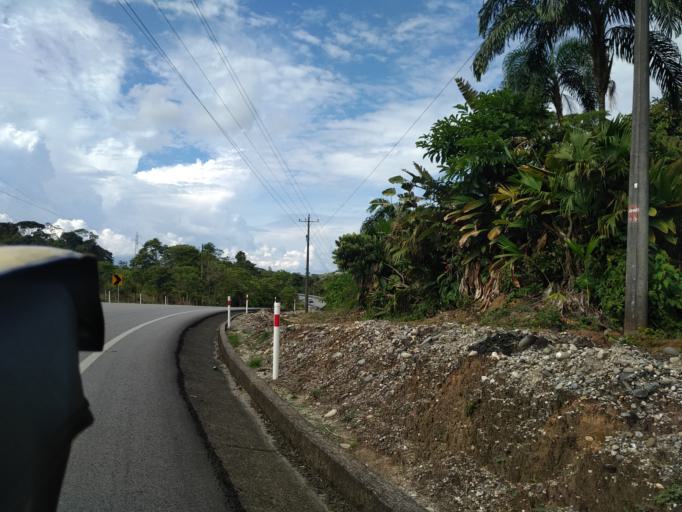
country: EC
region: Napo
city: Tena
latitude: -1.1136
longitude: -77.8080
